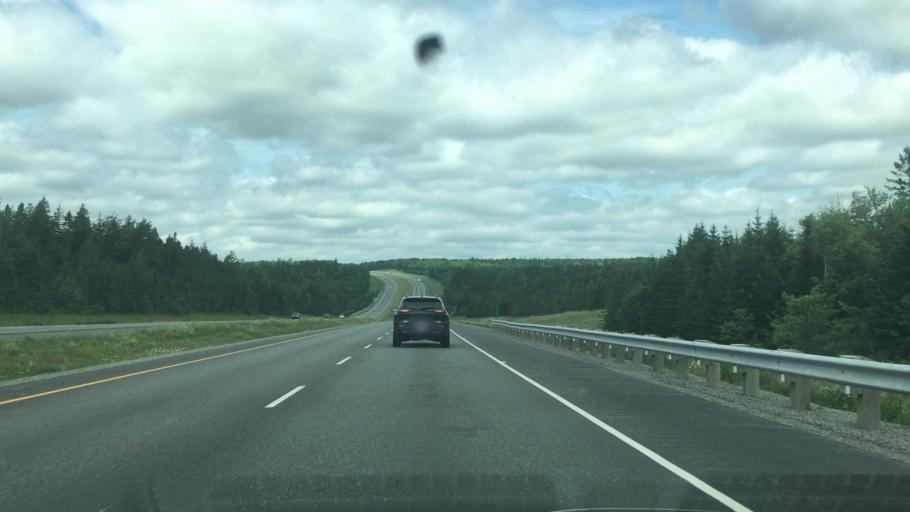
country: CA
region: Nova Scotia
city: Springhill
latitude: 45.7271
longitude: -64.0598
